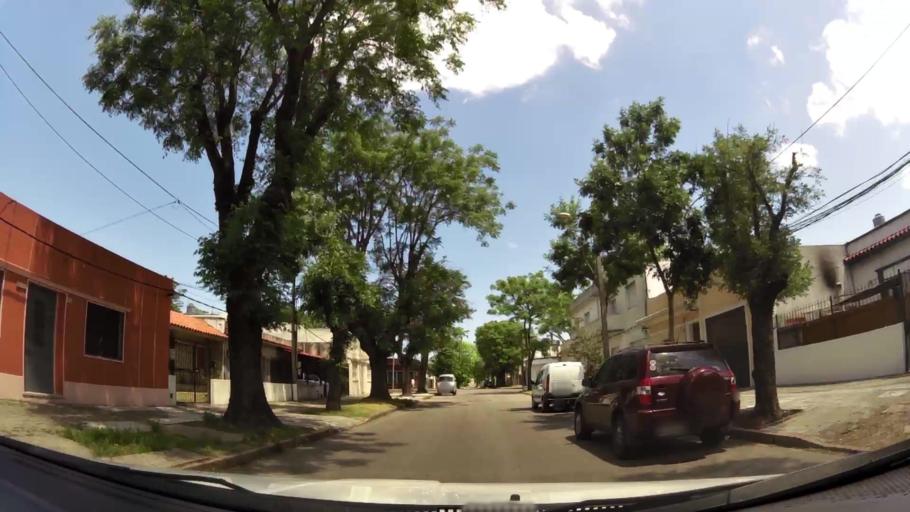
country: UY
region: Montevideo
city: Montevideo
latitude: -34.8656
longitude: -56.1890
